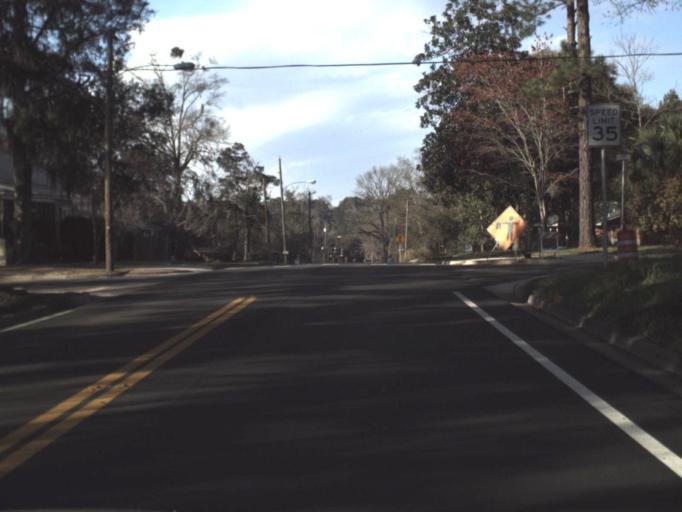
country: US
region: Florida
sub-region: Jackson County
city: Marianna
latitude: 30.7795
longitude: -85.2267
